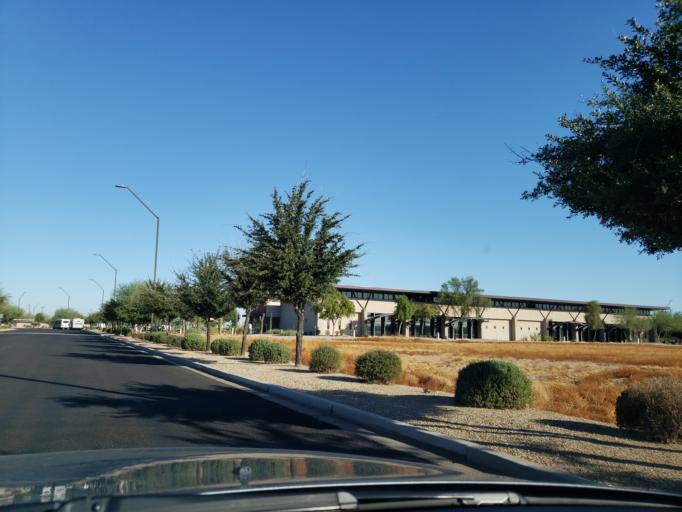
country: US
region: Arizona
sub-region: Maricopa County
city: Tolleson
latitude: 33.4440
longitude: -112.3027
